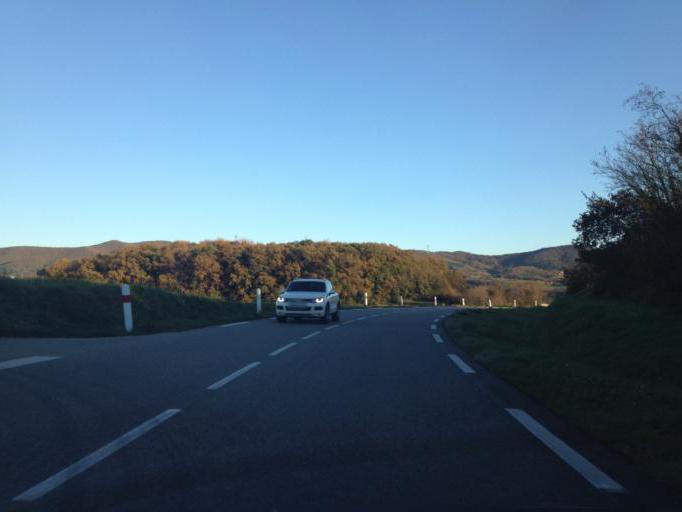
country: FR
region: Rhone-Alpes
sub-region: Departement de l'Ardeche
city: Chomerac
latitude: 44.6994
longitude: 4.7059
